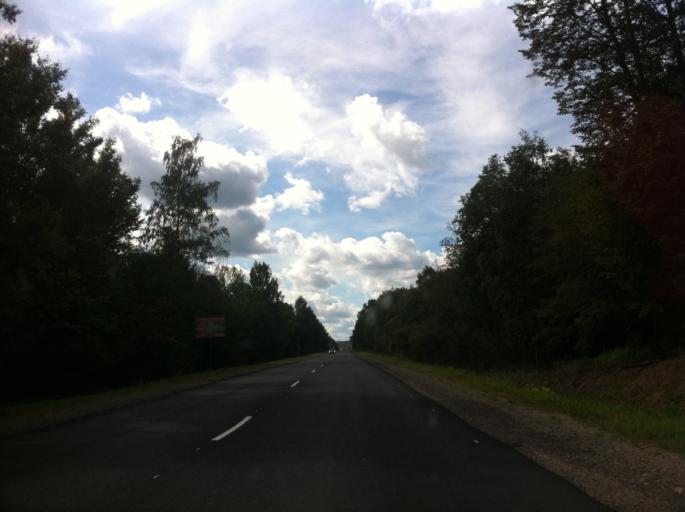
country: RU
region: Pskov
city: Izborsk
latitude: 57.7120
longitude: 27.9013
